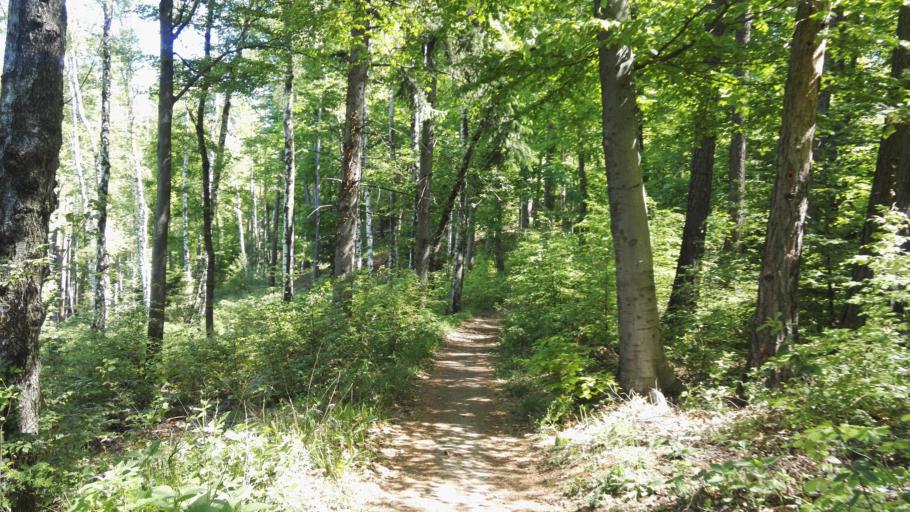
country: AT
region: Styria
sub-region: Politischer Bezirk Graz-Umgebung
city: Thal
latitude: 47.0807
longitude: 15.3760
